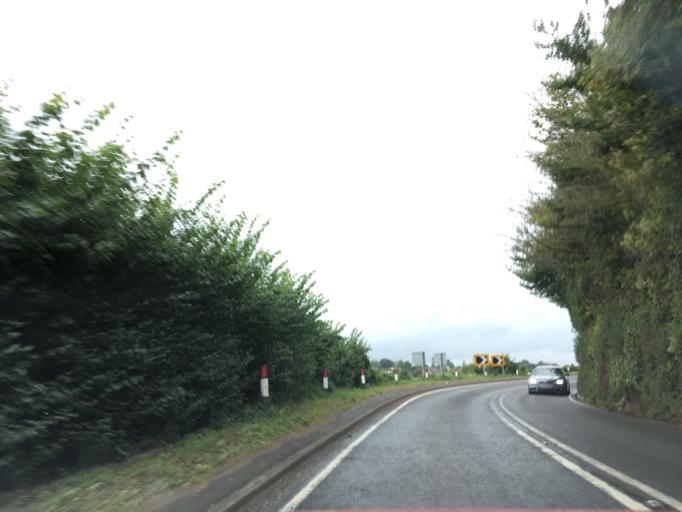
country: GB
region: England
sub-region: Herefordshire
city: Lea
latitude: 51.9009
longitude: -2.5242
